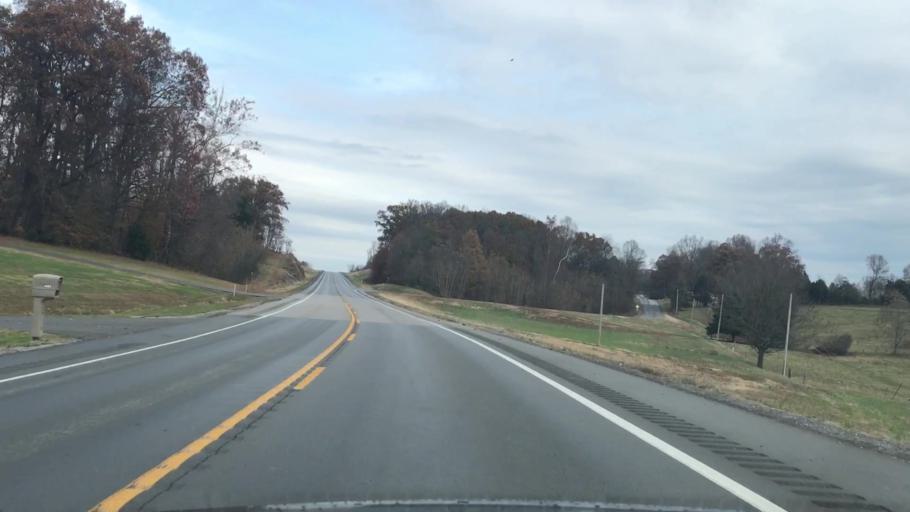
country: US
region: Kentucky
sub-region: Monroe County
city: Tompkinsville
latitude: 36.7612
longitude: -85.6862
